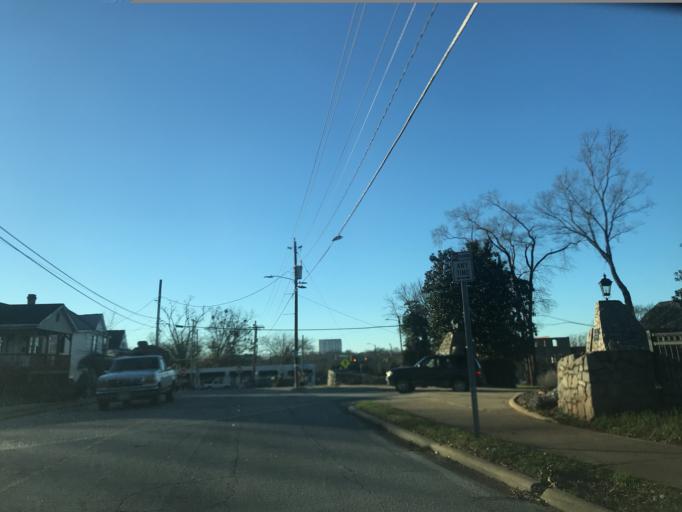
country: US
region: North Carolina
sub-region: Wake County
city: Raleigh
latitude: 35.7843
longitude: -78.6208
